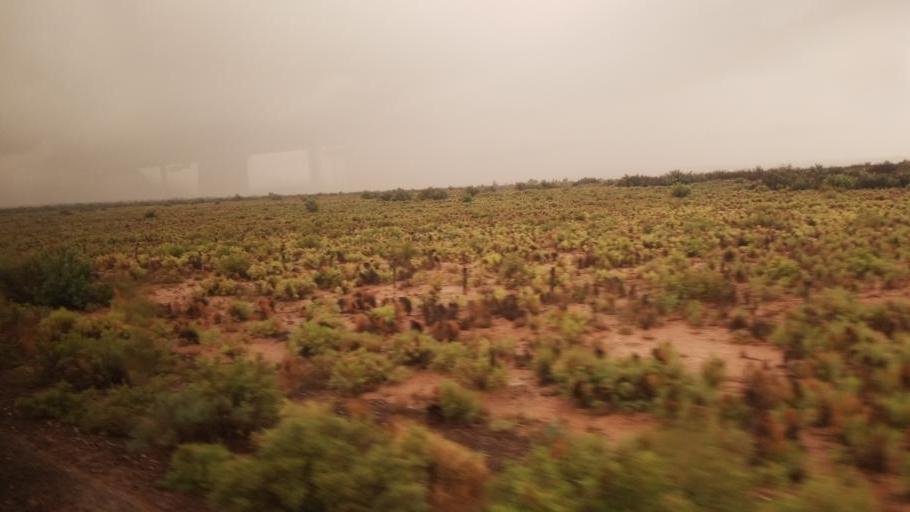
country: US
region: Arizona
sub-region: Navajo County
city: Joseph City
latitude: 34.9675
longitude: -110.4725
